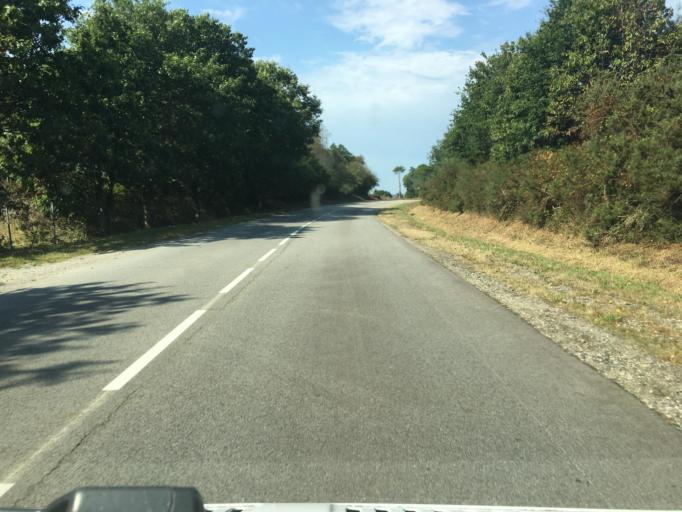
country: FR
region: Brittany
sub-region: Departement des Cotes-d'Armor
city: Mur-de-Bretagne
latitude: 48.2180
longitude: -3.0621
